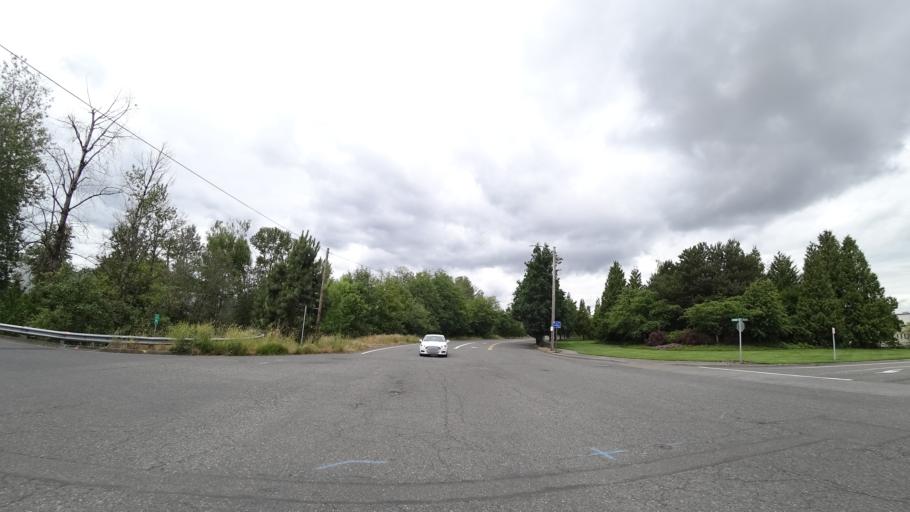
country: US
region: Washington
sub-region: Clark County
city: Vancouver
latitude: 45.5764
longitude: -122.6065
